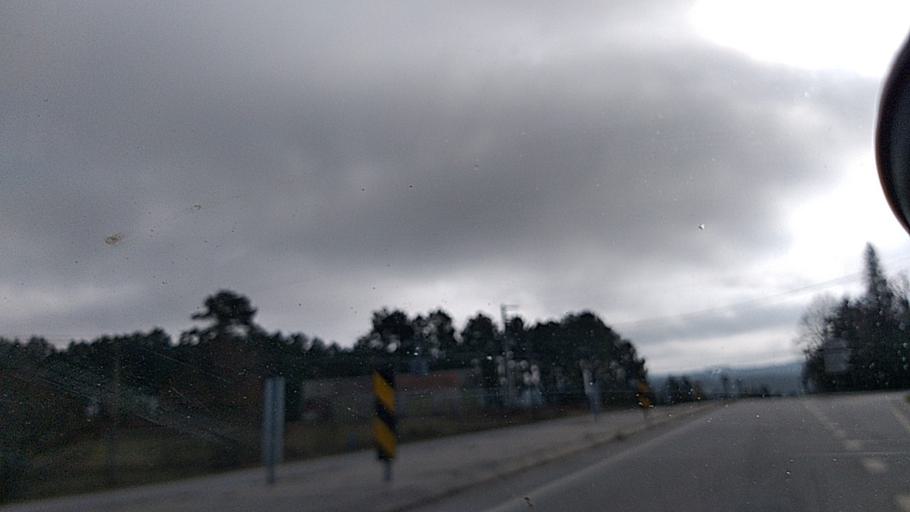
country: PT
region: Guarda
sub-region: Aguiar da Beira
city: Aguiar da Beira
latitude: 40.7900
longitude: -7.5070
